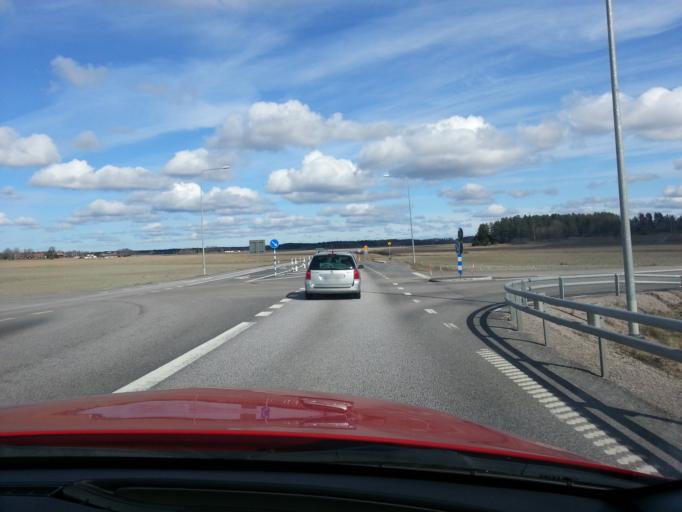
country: SE
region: Uppsala
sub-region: Uppsala Kommun
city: Vattholma
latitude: 59.9374
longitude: 17.8215
